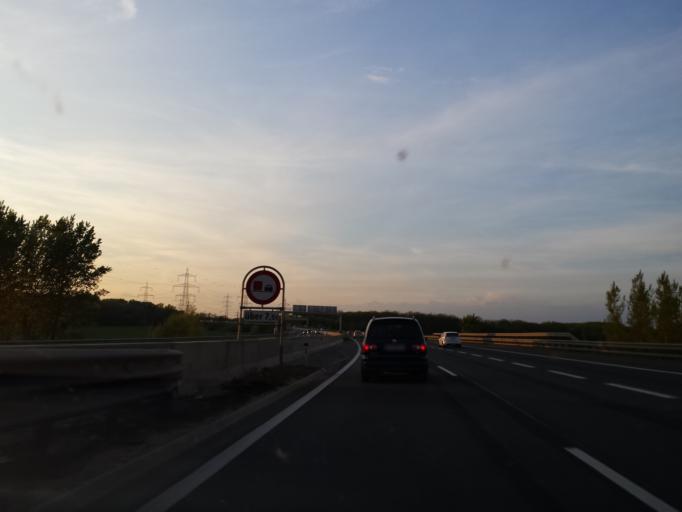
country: AT
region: Burgenland
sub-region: Politischer Bezirk Neusiedl am See
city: Parndorf
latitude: 48.0233
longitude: 16.8368
